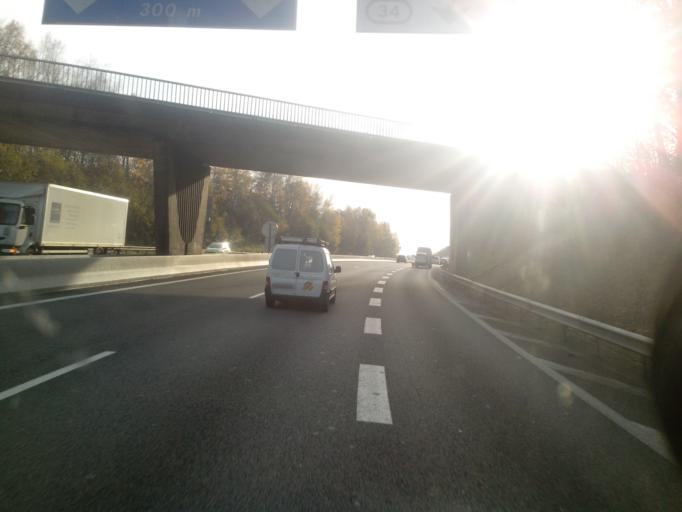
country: FR
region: Limousin
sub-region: Departement de la Haute-Vienne
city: Limoges
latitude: 45.8335
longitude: 1.2841
